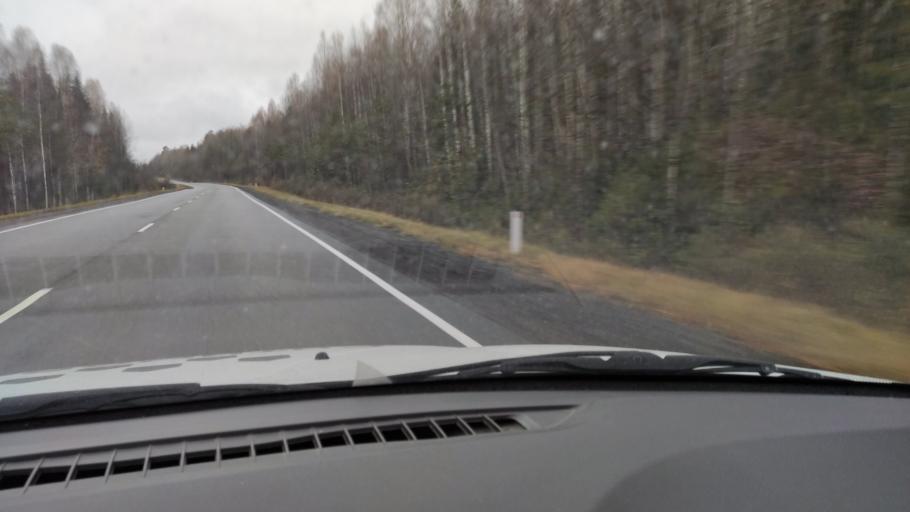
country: RU
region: Kirov
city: Chernaya Kholunitsa
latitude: 58.8675
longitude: 51.5655
